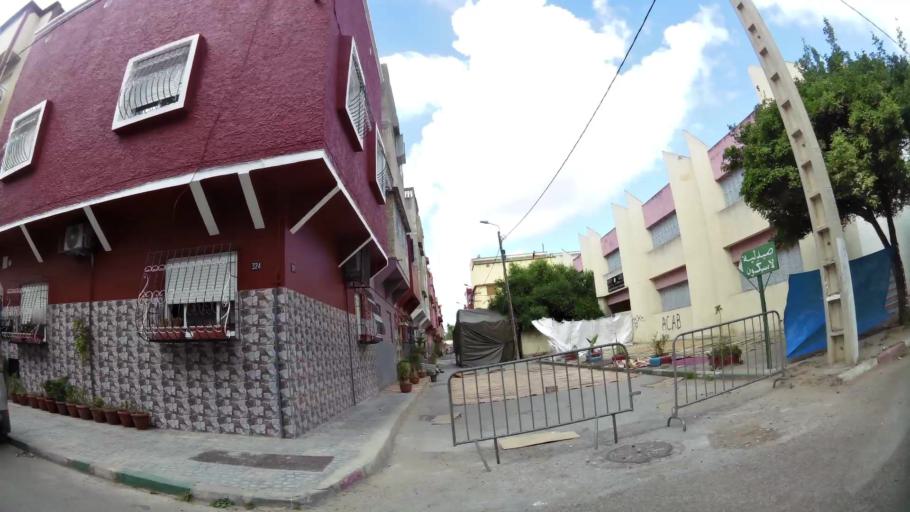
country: MA
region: Gharb-Chrarda-Beni Hssen
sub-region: Kenitra Province
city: Kenitra
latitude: 34.2591
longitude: -6.5679
